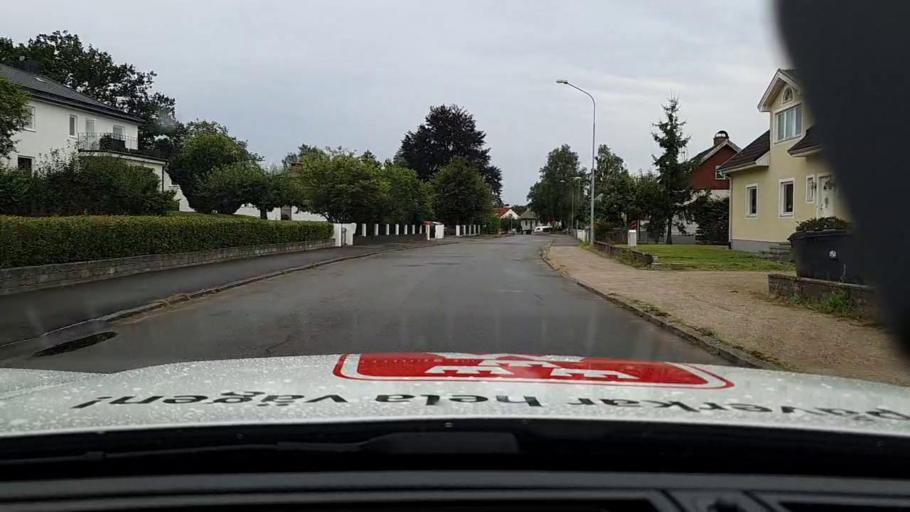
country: SE
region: Skane
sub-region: Hassleholms Kommun
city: Hassleholm
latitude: 56.1670
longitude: 13.7742
